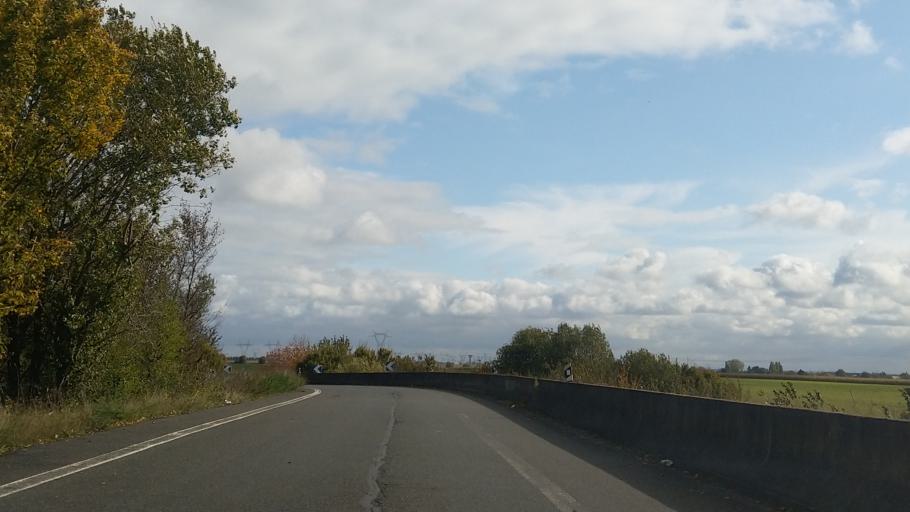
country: FR
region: Ile-de-France
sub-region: Departement du Val-d'Oise
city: Belloy-en-France
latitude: 49.0678
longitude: 2.3844
